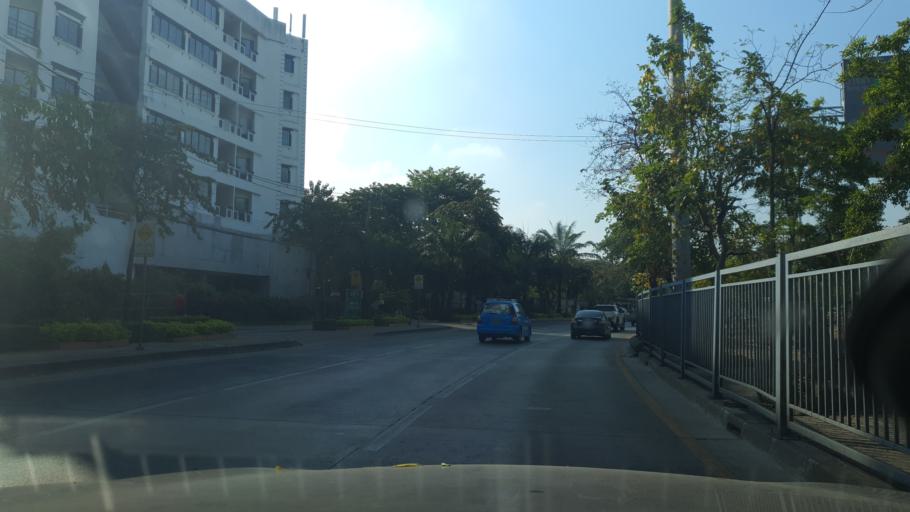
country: TH
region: Bangkok
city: Wang Thonglang
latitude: 13.7729
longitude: 100.6072
